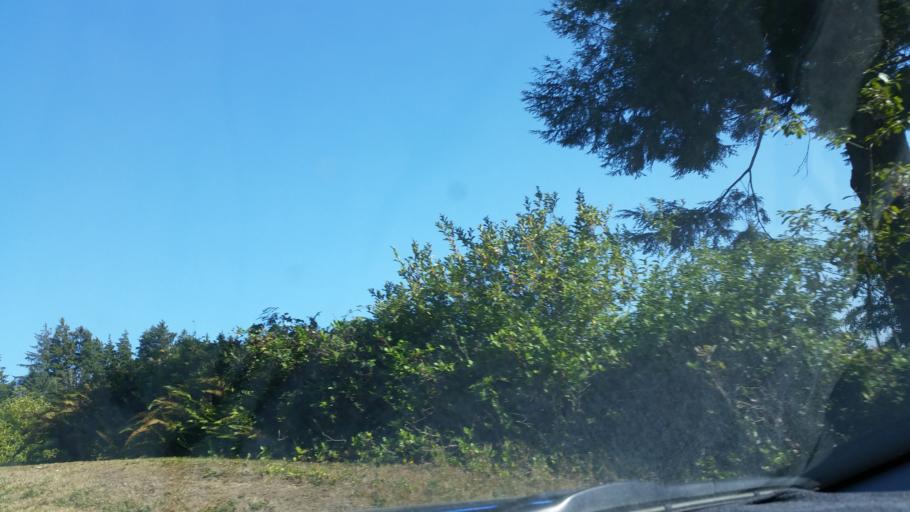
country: US
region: Oregon
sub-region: Clatsop County
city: Astoria
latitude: 46.1829
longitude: -123.8464
